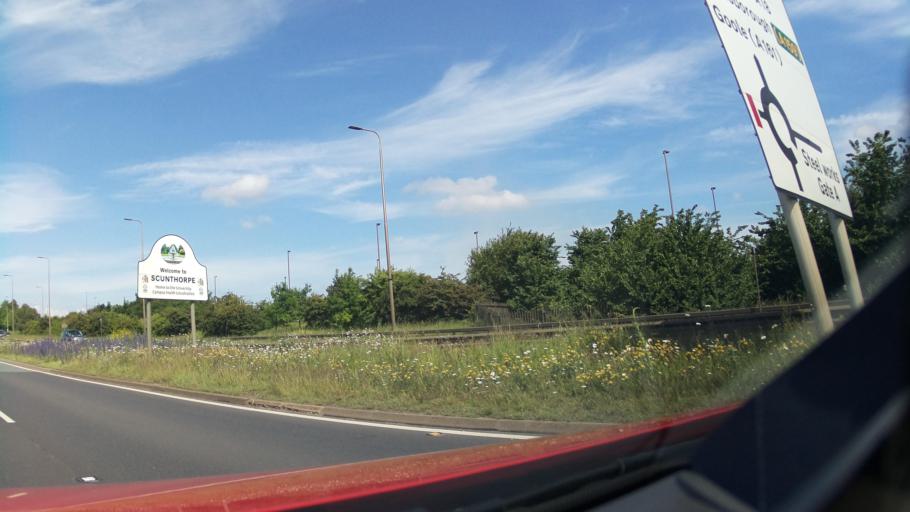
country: GB
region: England
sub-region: North Lincolnshire
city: Manton
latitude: 53.5635
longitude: -0.6048
